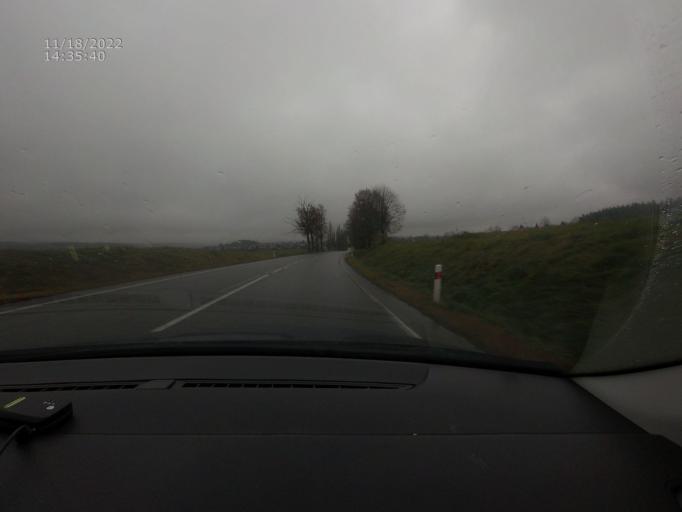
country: CZ
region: Jihocesky
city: Milevsko
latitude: 49.4556
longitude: 14.3455
